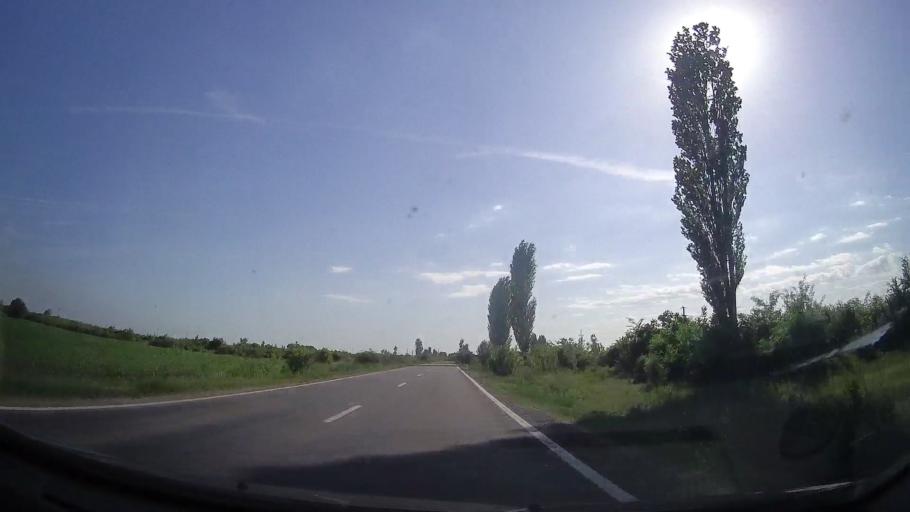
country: RO
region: Prahova
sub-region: Comuna Barcanesti
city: Barcanesti
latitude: 44.8974
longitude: 26.0583
